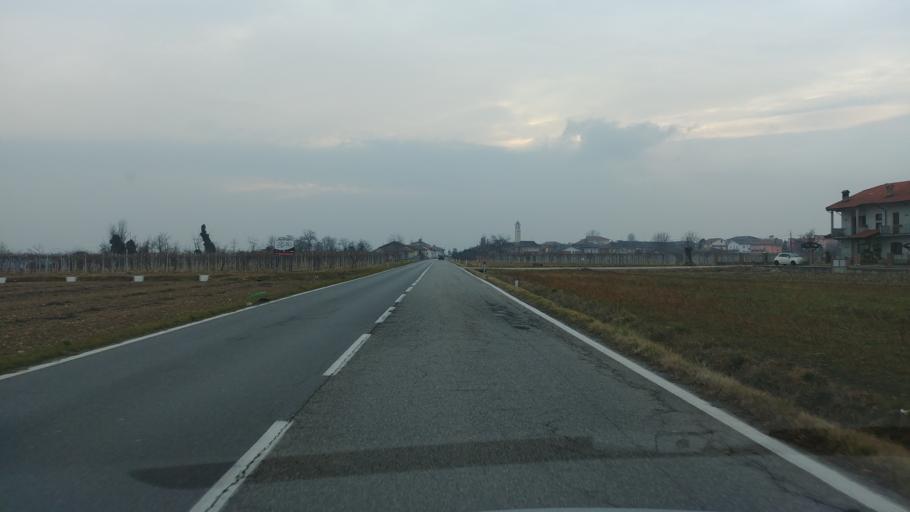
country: IT
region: Piedmont
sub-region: Provincia di Cuneo
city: Castelletto Stura
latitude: 44.4367
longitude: 7.5947
